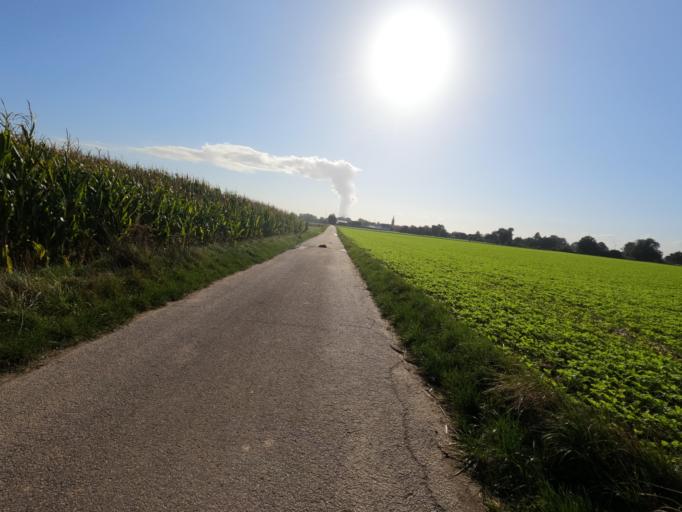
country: DE
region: North Rhine-Westphalia
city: Siersdorf
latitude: 50.9117
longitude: 6.2516
